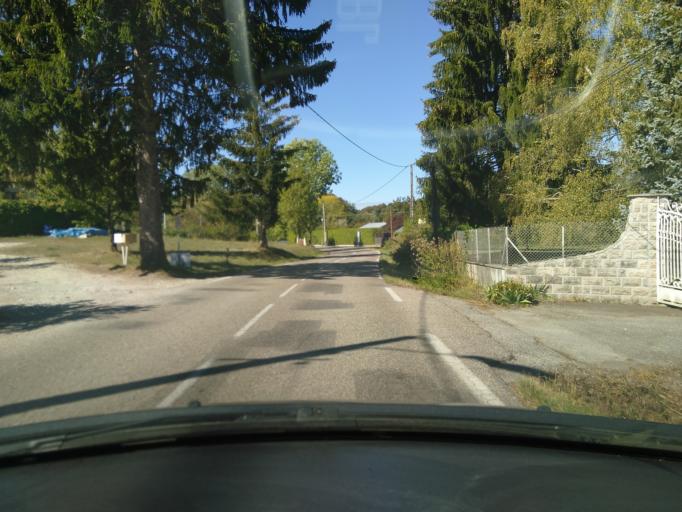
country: FR
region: Rhone-Alpes
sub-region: Departement de l'Isere
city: Saint-Cassien
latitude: 45.3667
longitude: 5.5489
